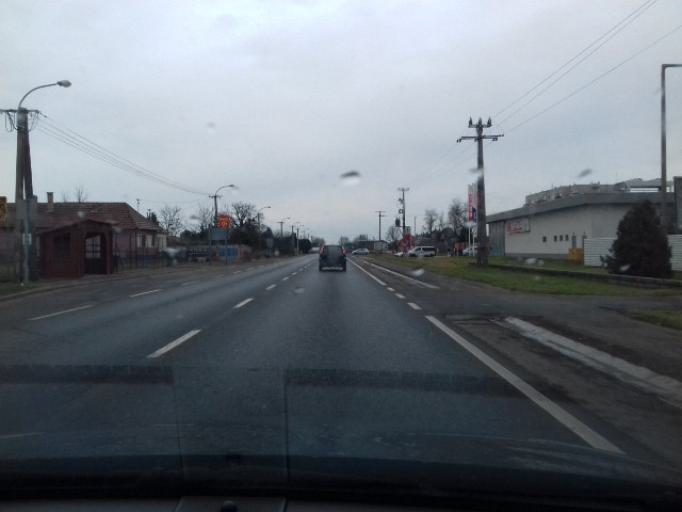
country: HU
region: Szabolcs-Szatmar-Bereg
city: Ujfeherto
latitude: 47.8168
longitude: 21.7006
